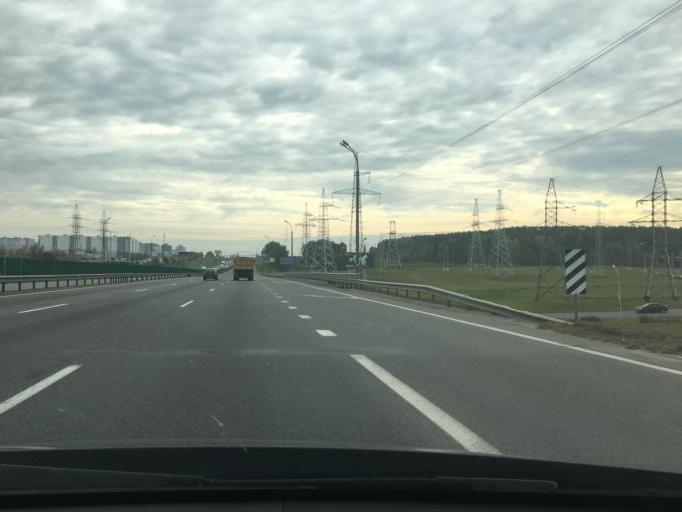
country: BY
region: Minsk
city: Malinovka
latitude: 53.8714
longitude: 27.4217
